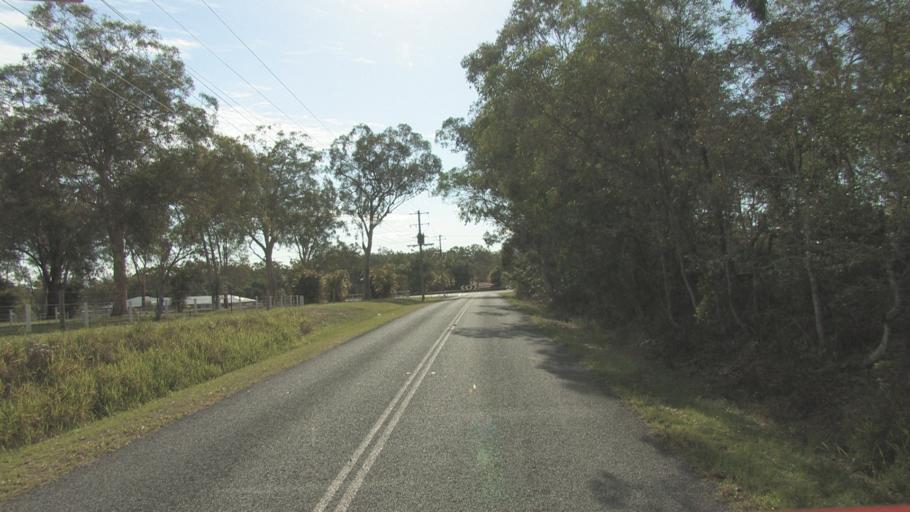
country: AU
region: Queensland
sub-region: Logan
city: Logan Reserve
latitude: -27.7328
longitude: 153.0790
